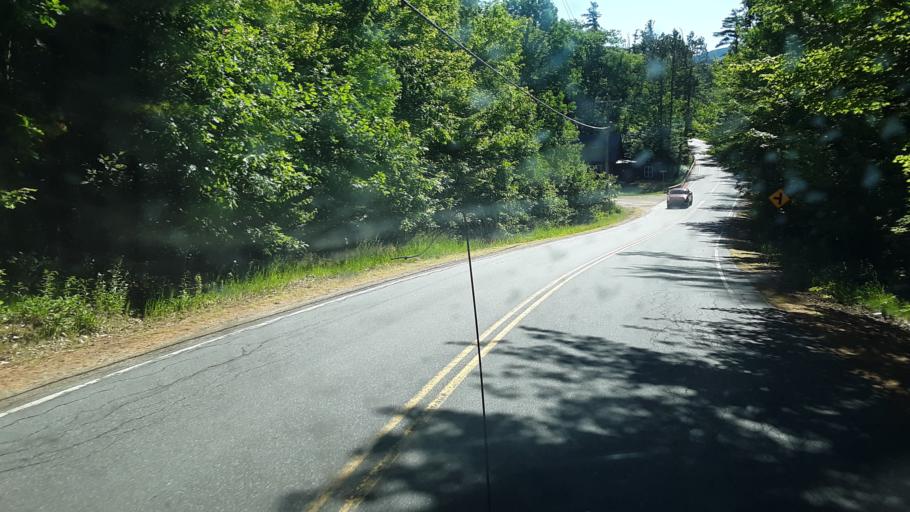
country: US
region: New Hampshire
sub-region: Grafton County
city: North Haverhill
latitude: 44.0869
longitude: -71.9620
